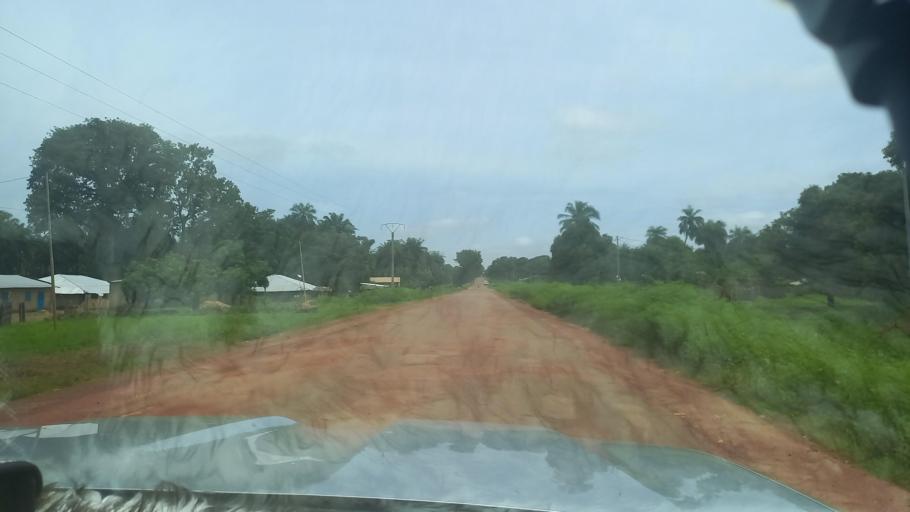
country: SN
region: Kolda
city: Marsassoum
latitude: 12.9666
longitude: -15.9617
